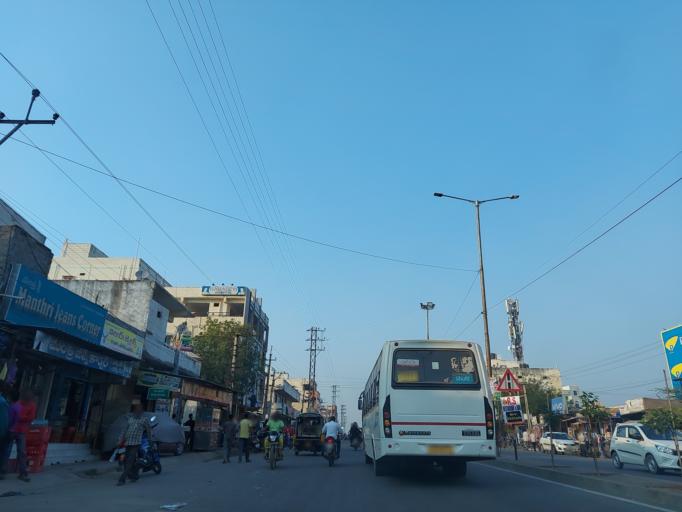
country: IN
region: Telangana
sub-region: Rangareddi
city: Balapur
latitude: 17.2068
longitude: 78.4765
